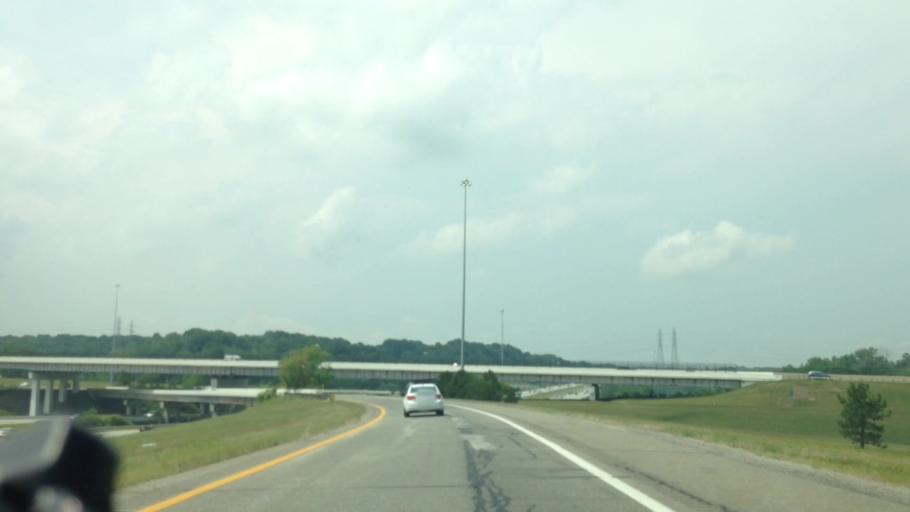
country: US
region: Ohio
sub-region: Cuyahoga County
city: Seven Hills
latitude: 41.4077
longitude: -81.6433
